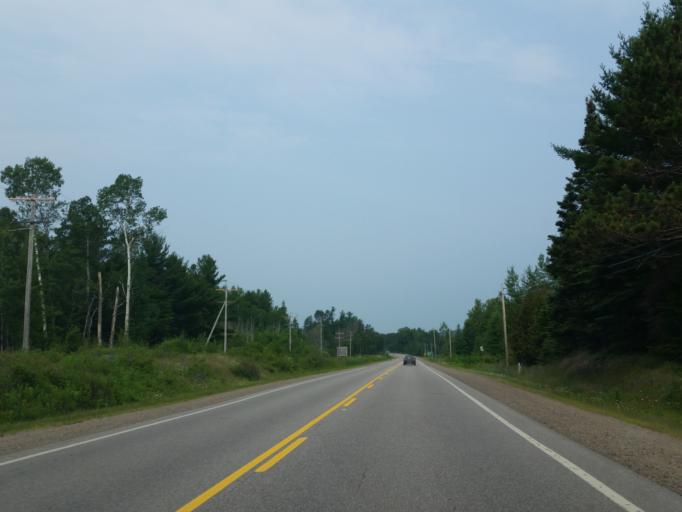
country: CA
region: Ontario
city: Petawawa
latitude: 45.5012
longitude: -77.6045
